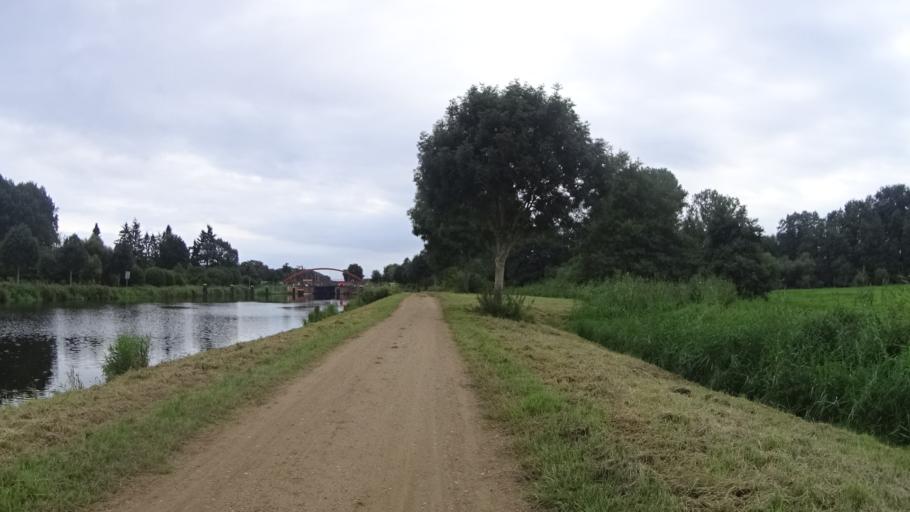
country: DE
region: Schleswig-Holstein
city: Kuhsen
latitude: 53.6756
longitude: 10.6355
